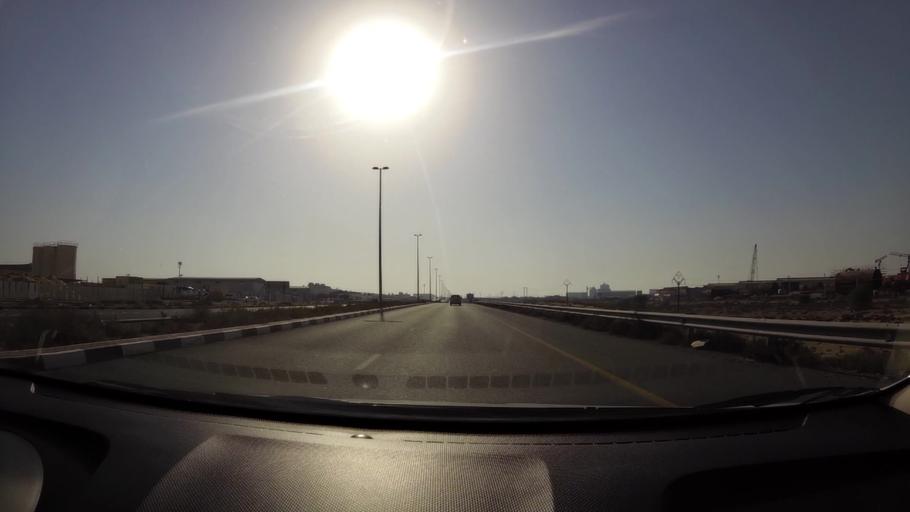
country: AE
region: Umm al Qaywayn
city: Umm al Qaywayn
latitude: 25.4345
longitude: 55.5700
